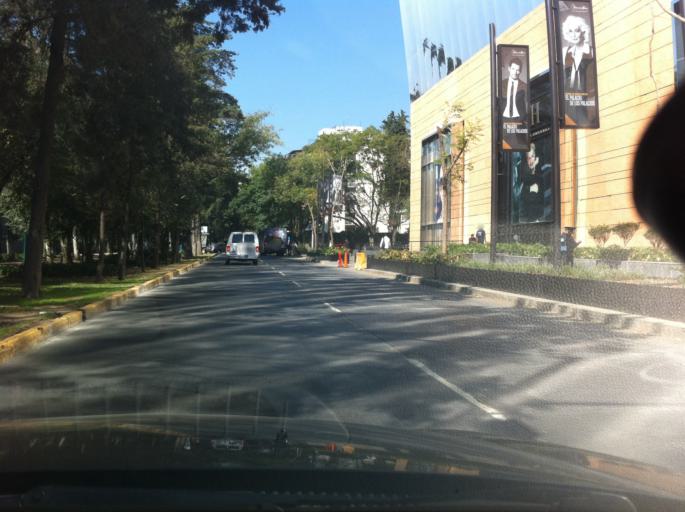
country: MX
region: Mexico City
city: Miguel Hidalgo
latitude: 19.4346
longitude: -99.2023
